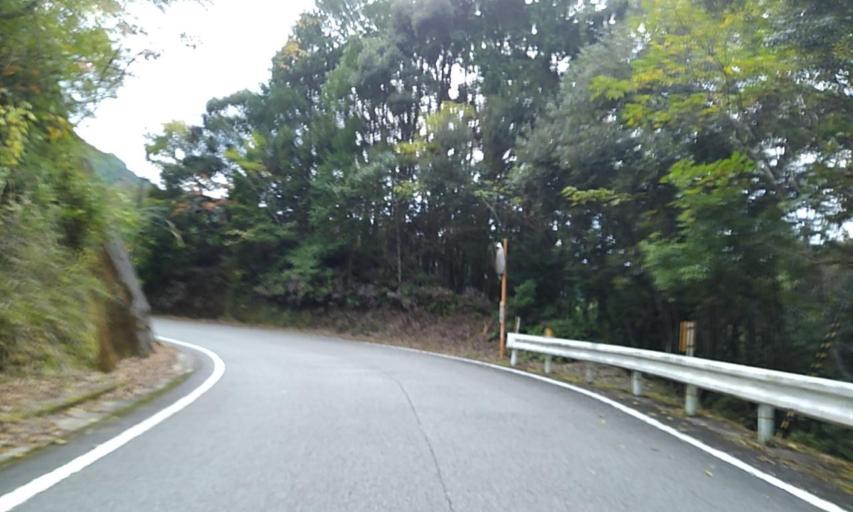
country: JP
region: Wakayama
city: Shingu
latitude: 33.5426
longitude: 135.8309
